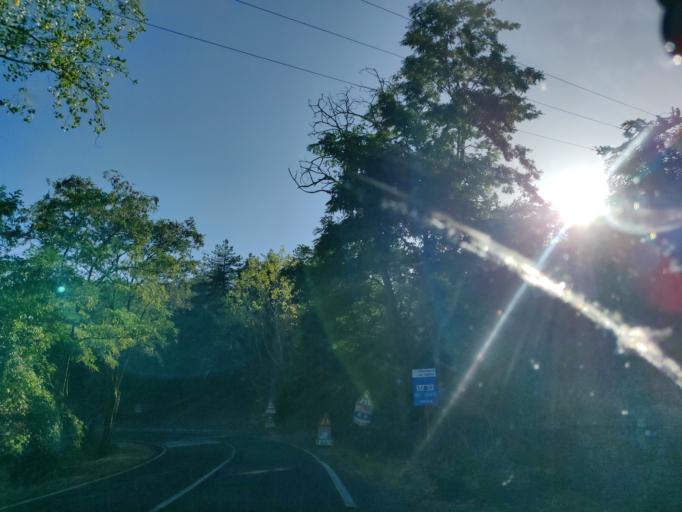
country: IT
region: Tuscany
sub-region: Provincia di Siena
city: Abbadia San Salvatore
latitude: 42.8741
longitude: 11.6832
